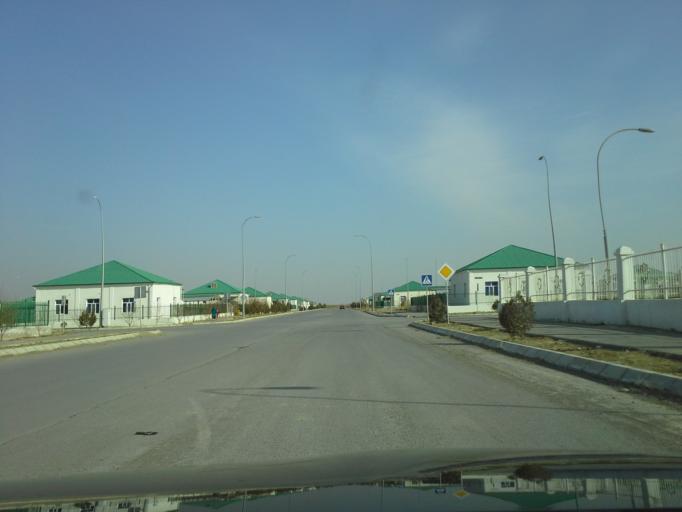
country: TM
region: Ahal
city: Abadan
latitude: 38.1713
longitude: 58.0487
